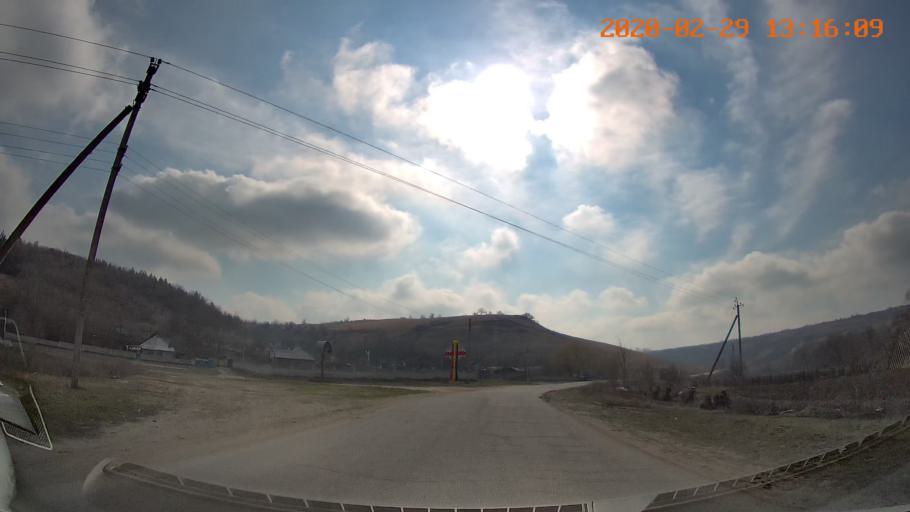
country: MD
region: Telenesti
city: Camenca
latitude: 48.0046
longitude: 28.6664
